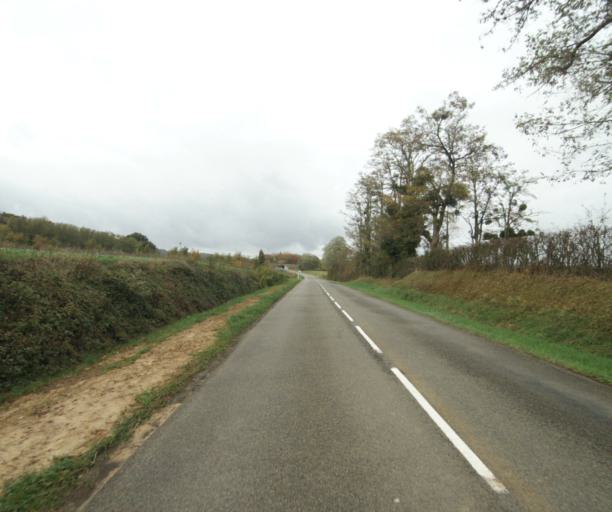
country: FR
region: Rhone-Alpes
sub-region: Departement de l'Ain
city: Pont-de-Vaux
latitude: 46.4593
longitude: 4.8817
